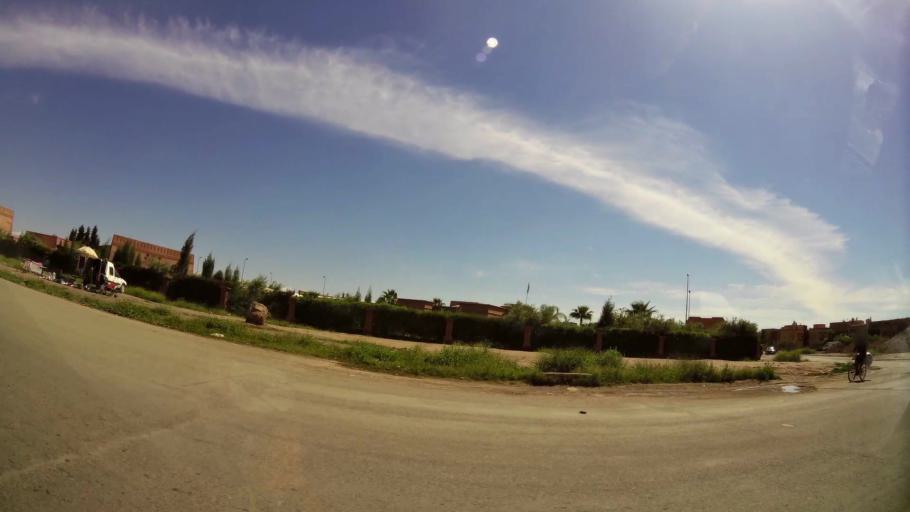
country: MA
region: Marrakech-Tensift-Al Haouz
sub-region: Marrakech
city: Marrakesh
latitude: 31.6407
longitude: -8.1040
